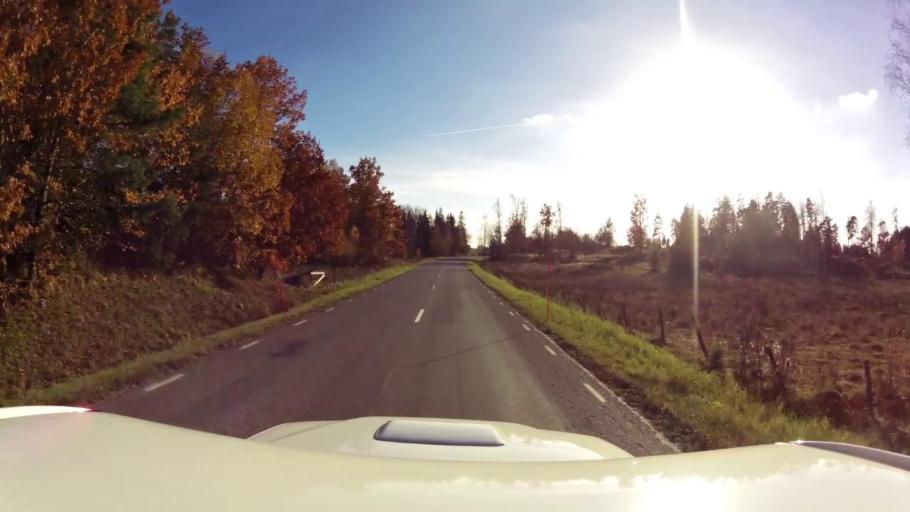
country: SE
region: OEstergoetland
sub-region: Linkopings Kommun
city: Vikingstad
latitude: 58.3111
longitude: 15.4904
